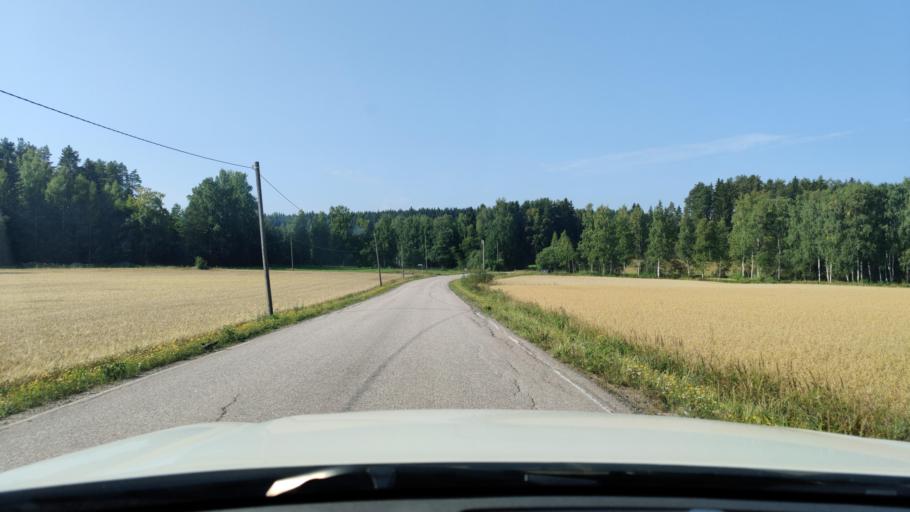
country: FI
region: Haeme
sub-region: Riihimaeki
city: Riihimaeki
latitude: 60.6886
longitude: 24.6727
